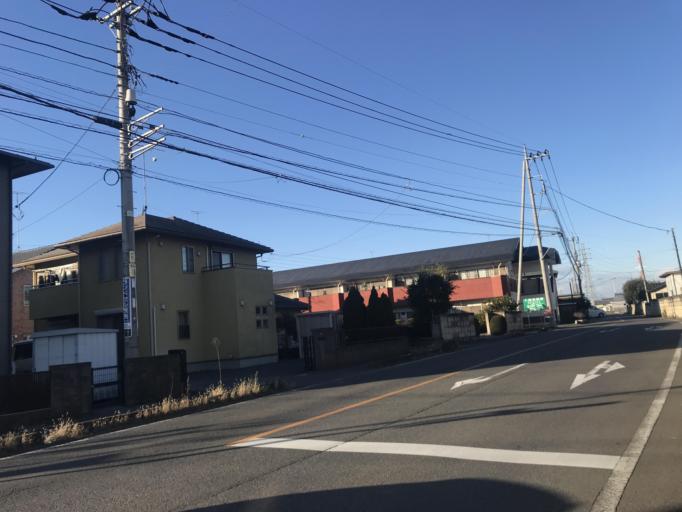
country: JP
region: Tochigi
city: Kaminokawa
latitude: 36.4383
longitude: 139.8711
